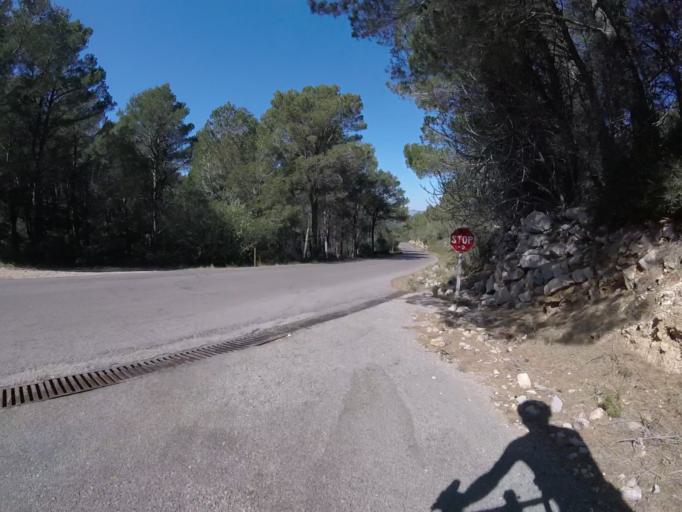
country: ES
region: Valencia
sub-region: Provincia de Castello
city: Cervera del Maestre
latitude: 40.4076
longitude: 0.1967
